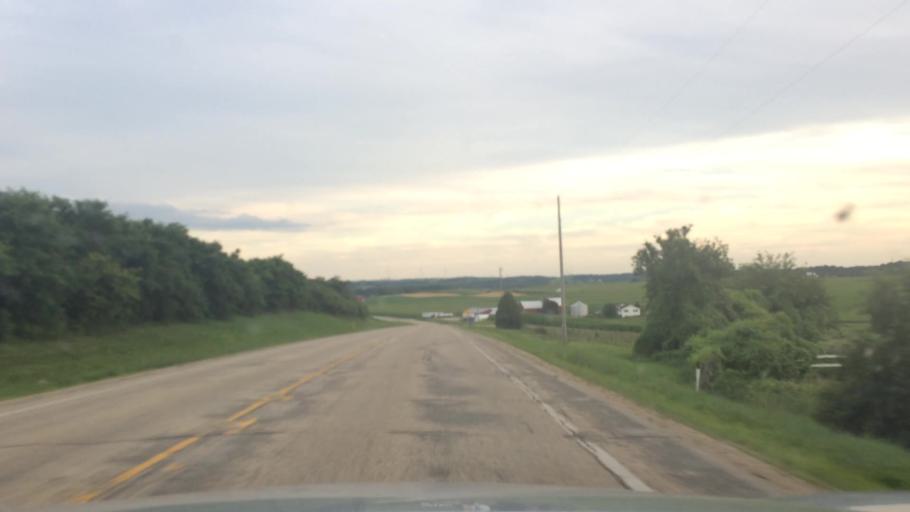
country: US
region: Wisconsin
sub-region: Columbia County
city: Lodi
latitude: 43.2261
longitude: -89.5438
